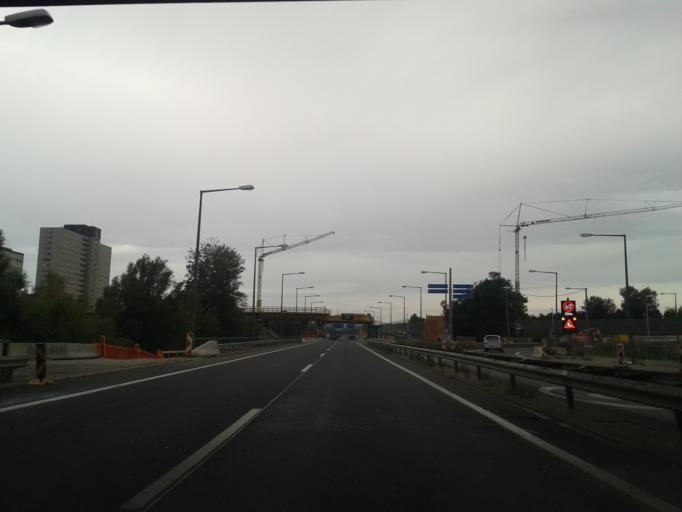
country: AT
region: Vienna
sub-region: Wien Stadt
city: Vienna
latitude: 48.1934
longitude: 16.4168
